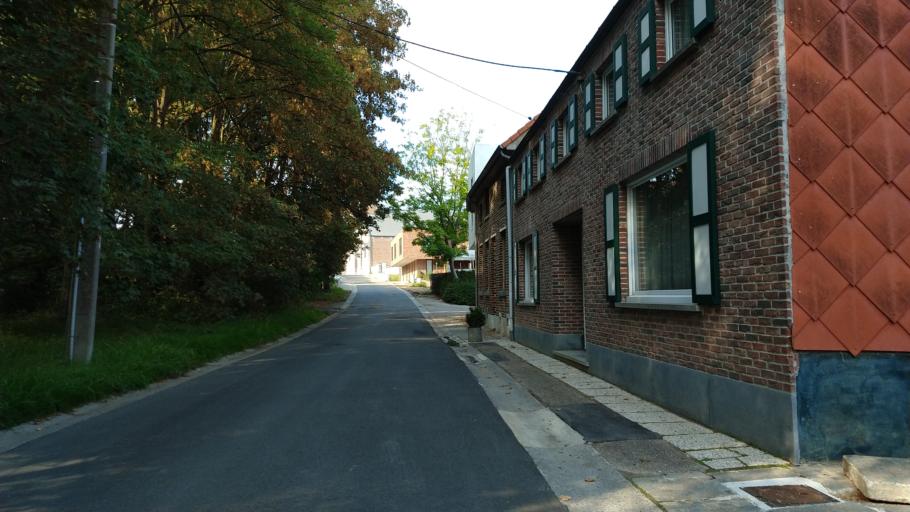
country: BE
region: Flanders
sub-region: Provincie Vlaams-Brabant
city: Boutersem
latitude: 50.8375
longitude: 4.8319
